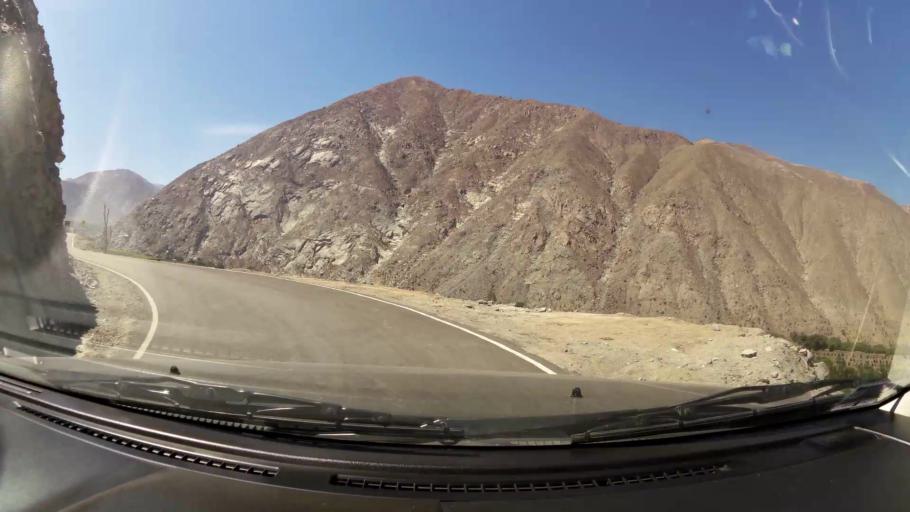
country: PE
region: Ica
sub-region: Provincia de Pisco
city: Huancano
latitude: -13.8312
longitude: -75.5422
